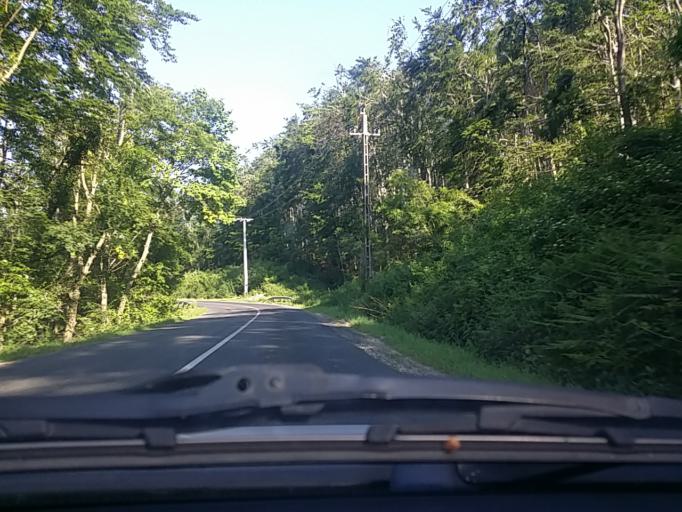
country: HU
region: Pest
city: Pilisszentkereszt
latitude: 47.7128
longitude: 18.8761
